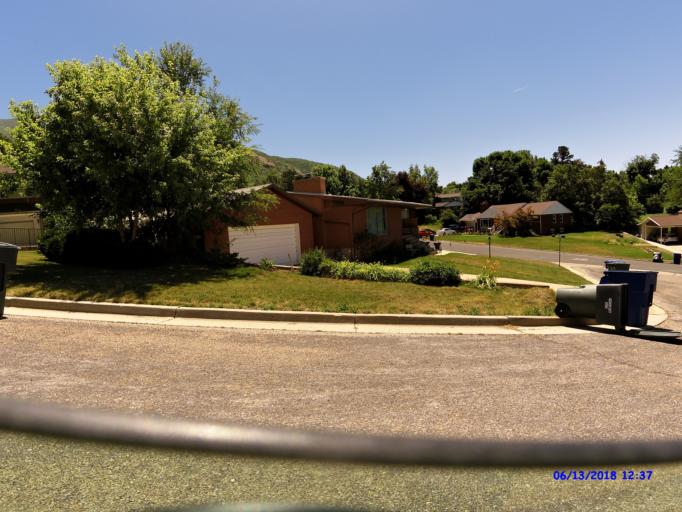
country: US
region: Utah
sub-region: Weber County
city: South Ogden
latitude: 41.1993
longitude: -111.9399
